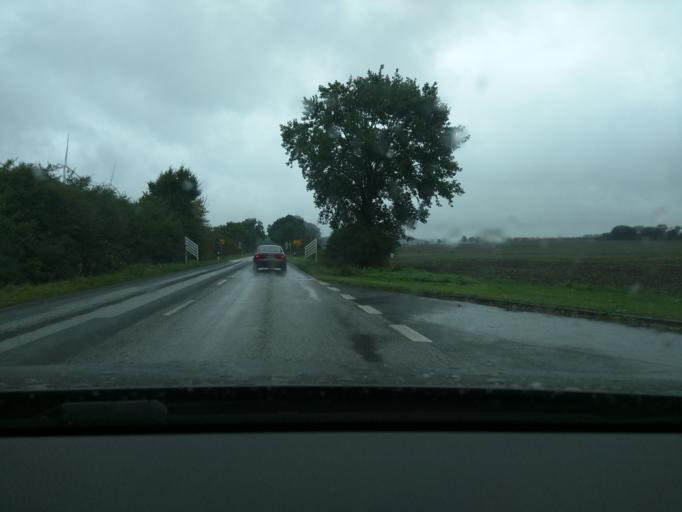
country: DE
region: Schleswig-Holstein
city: Lutau
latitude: 53.4391
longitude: 10.5554
